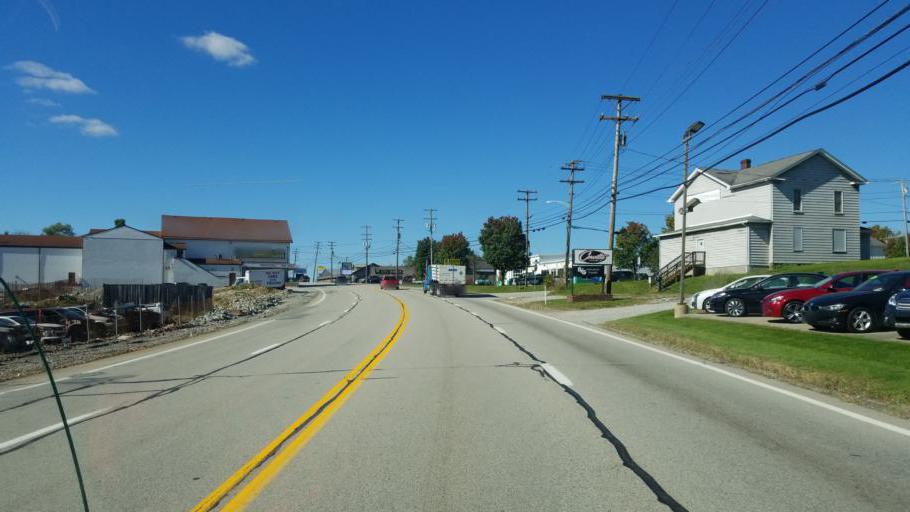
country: US
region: Pennsylvania
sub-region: Westmoreland County
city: Irwin
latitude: 40.3367
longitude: -79.7457
